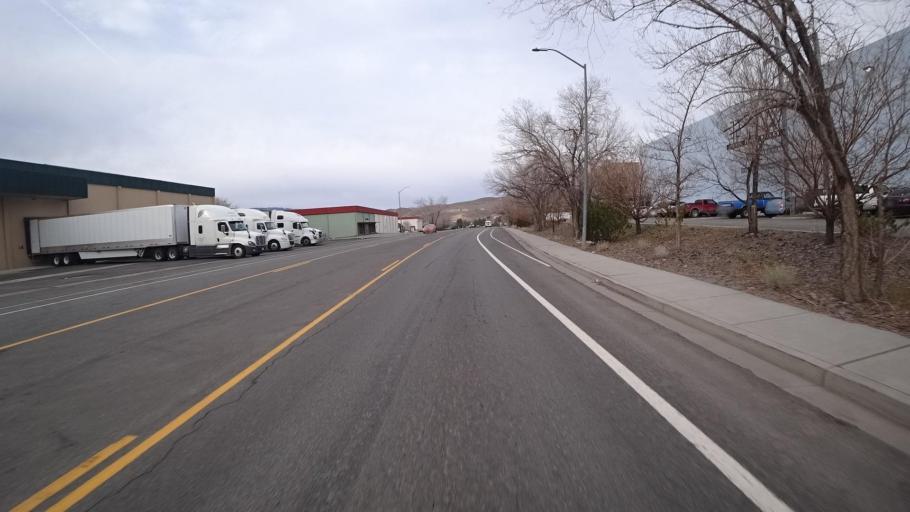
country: US
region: Nevada
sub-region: Washoe County
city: Reno
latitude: 39.5703
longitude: -119.8152
